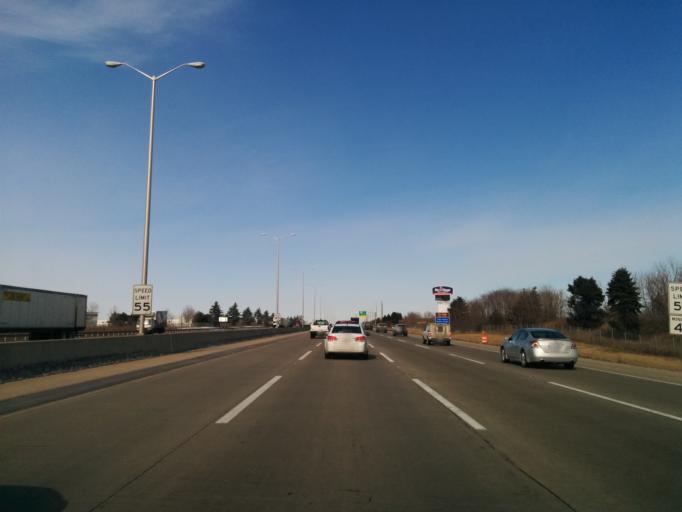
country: US
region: Illinois
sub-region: Lake County
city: Gurnee
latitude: 42.3668
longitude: -87.9404
